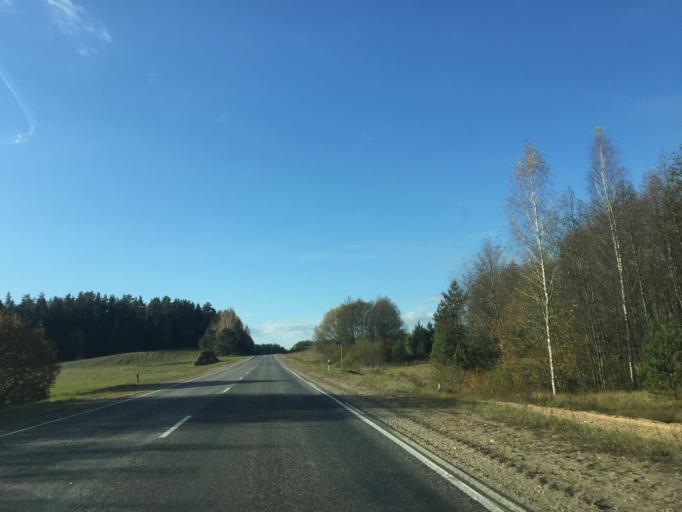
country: BY
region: Minsk
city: Myadzyel
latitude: 55.0507
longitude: 27.0961
